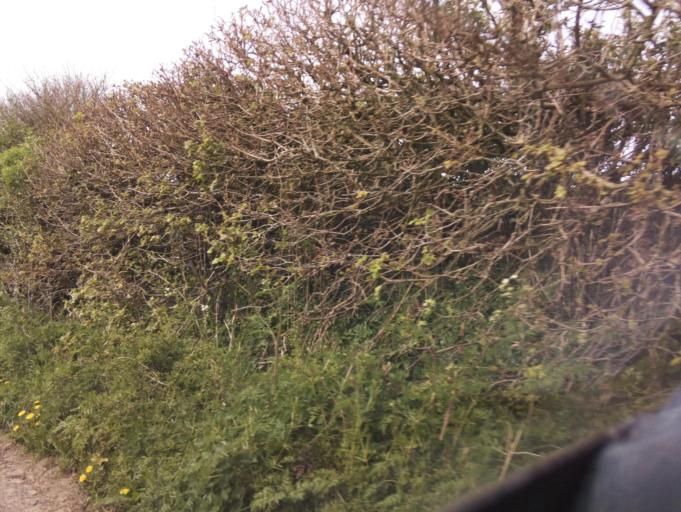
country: GB
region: England
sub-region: Dorset
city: Sherborne
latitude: 50.9685
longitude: -2.5038
